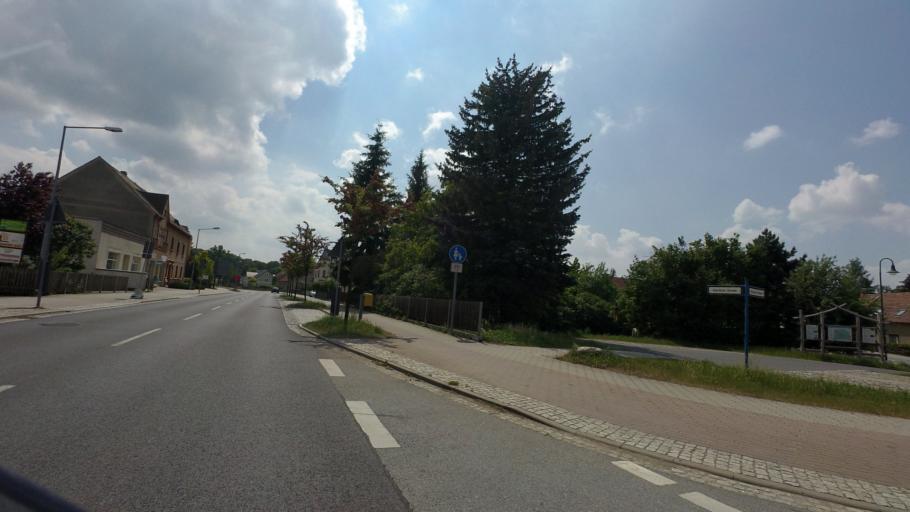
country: DE
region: Saxony
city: Rietschen
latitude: 51.3953
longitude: 14.7857
